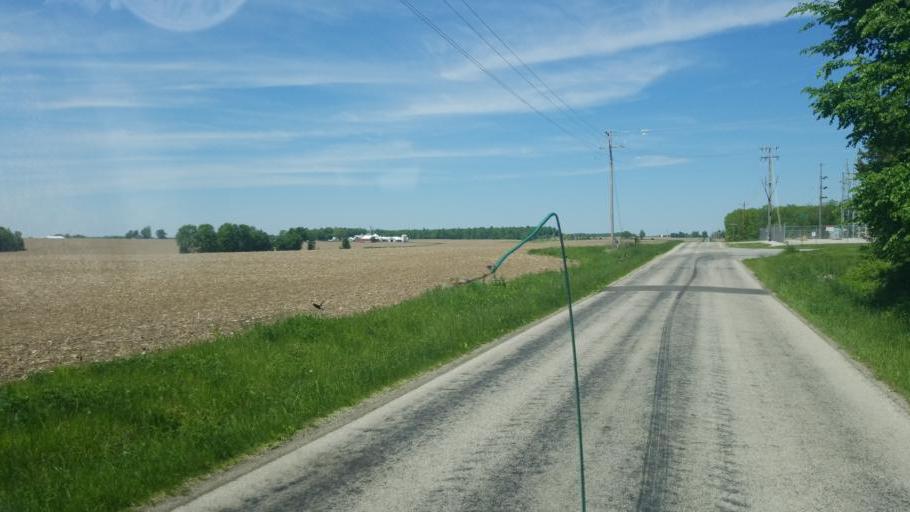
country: US
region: Ohio
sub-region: Huron County
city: Greenwich
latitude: 41.0936
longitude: -82.5372
